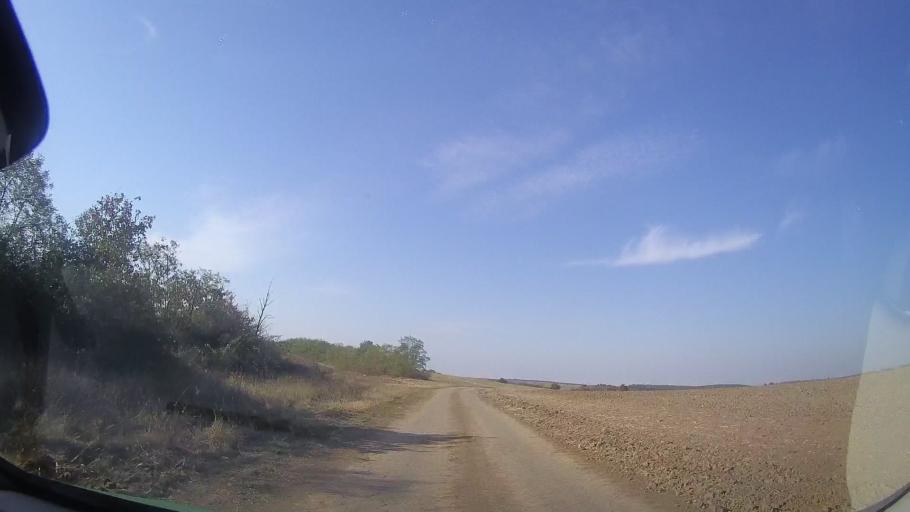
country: RO
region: Timis
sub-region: Comuna Bogda
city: Bogda
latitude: 45.8957
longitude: 21.5634
